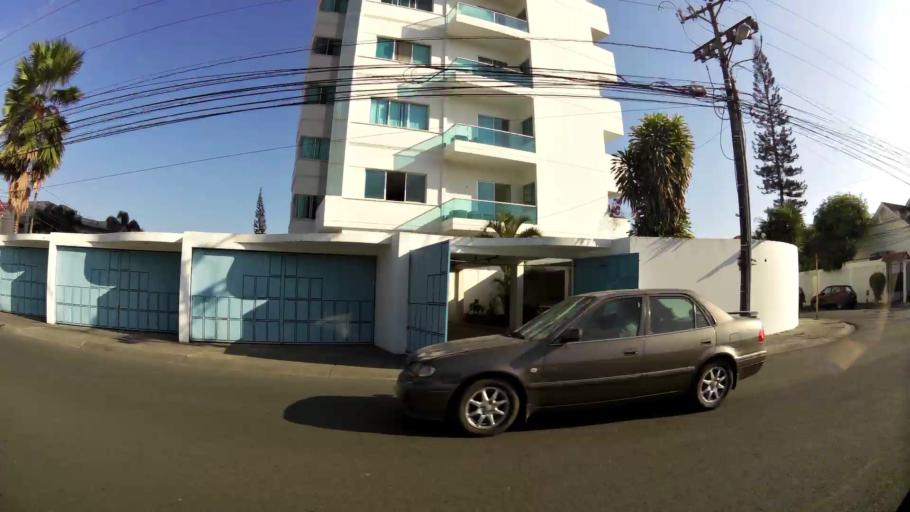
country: EC
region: Guayas
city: Santa Lucia
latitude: -2.1879
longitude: -79.9665
